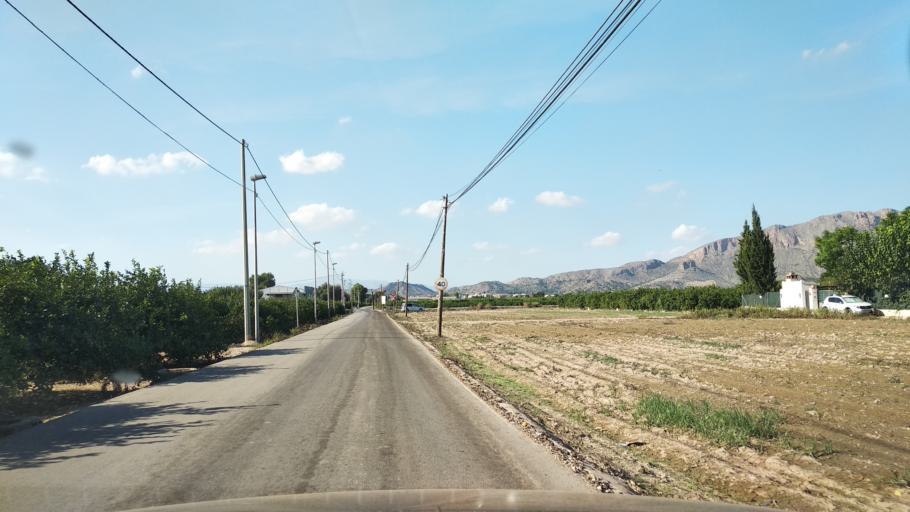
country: ES
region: Murcia
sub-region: Murcia
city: Santomera
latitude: 38.0462
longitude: -1.0377
